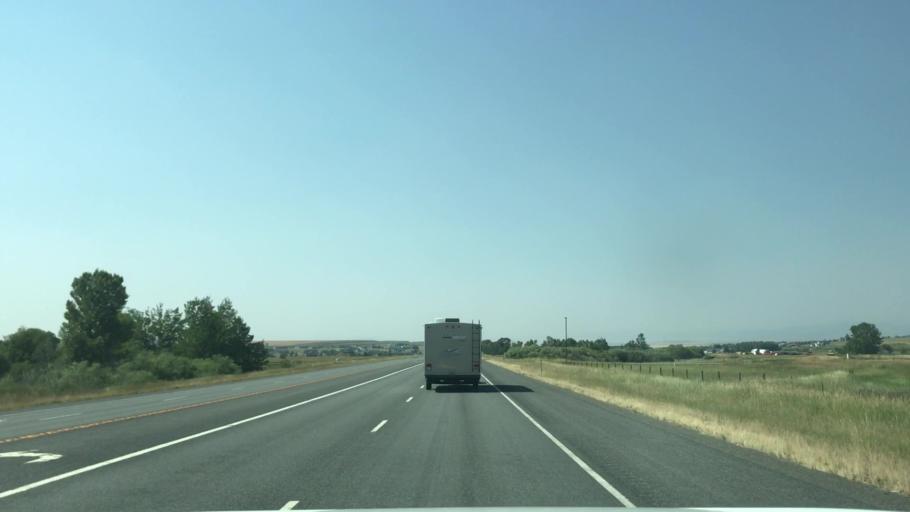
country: US
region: Montana
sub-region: Lewis and Clark County
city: East Helena
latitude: 46.5365
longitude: -111.7279
